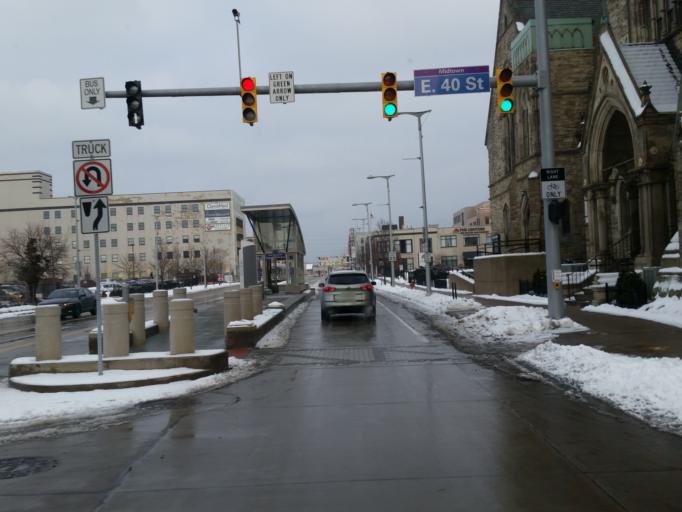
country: US
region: Ohio
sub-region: Cuyahoga County
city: Cleveland
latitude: 41.5035
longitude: -81.6578
